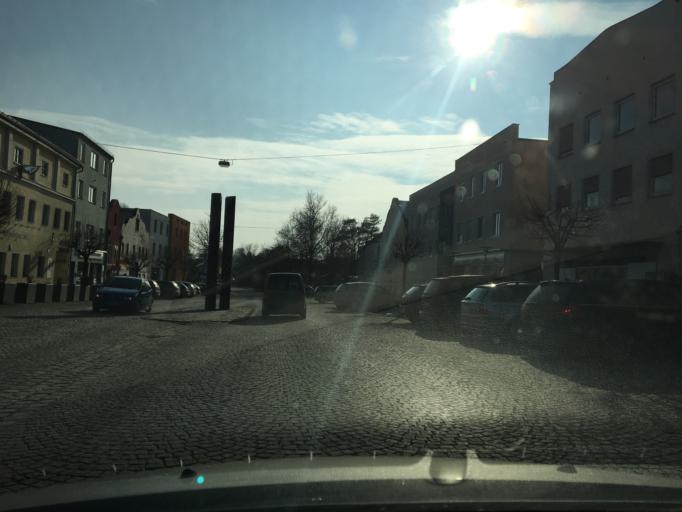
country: DE
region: Bavaria
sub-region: Lower Bavaria
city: Gangkofen
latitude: 48.4371
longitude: 12.5634
